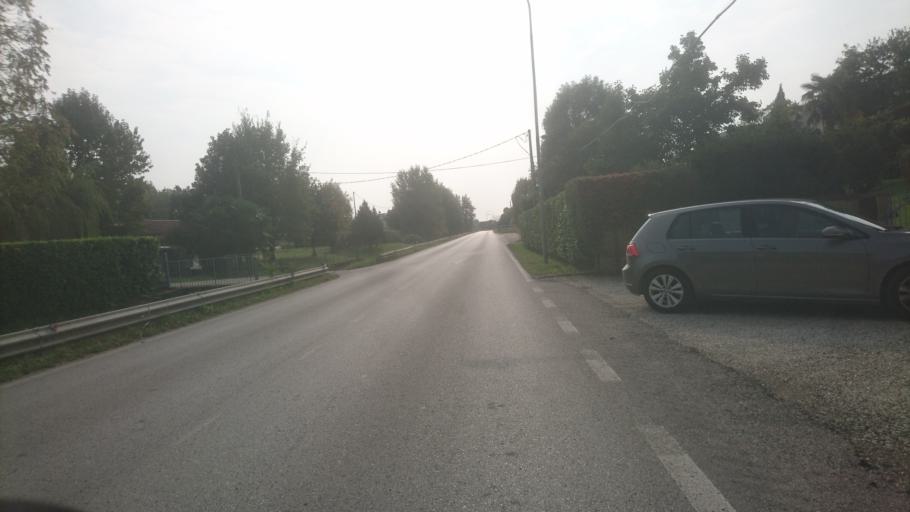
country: IT
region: Veneto
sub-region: Provincia di Vicenza
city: Quinto Vicentino
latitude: 45.5778
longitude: 11.6456
